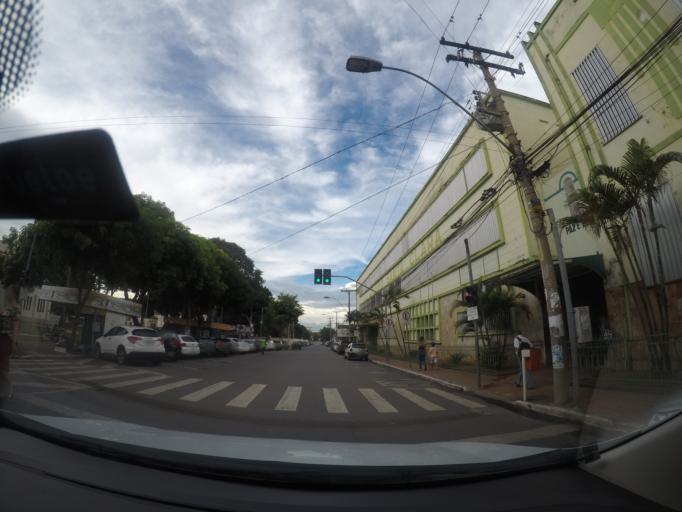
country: BR
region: Goias
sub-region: Goiania
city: Goiania
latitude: -16.6665
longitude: -49.2936
